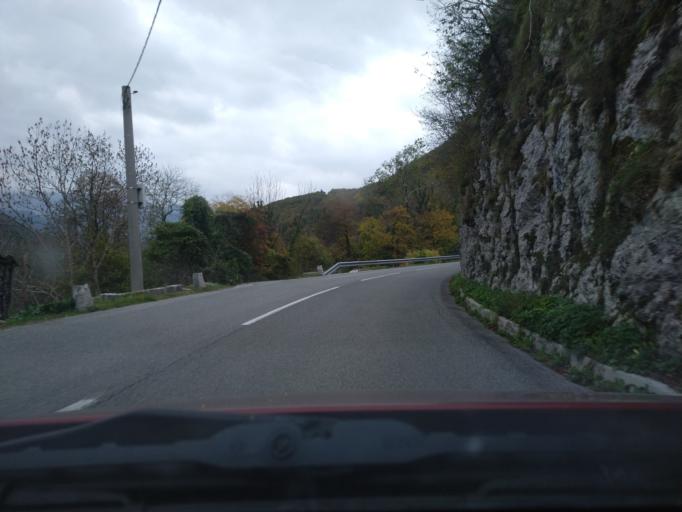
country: SI
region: Kobarid
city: Kobarid
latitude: 46.2791
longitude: 13.5543
